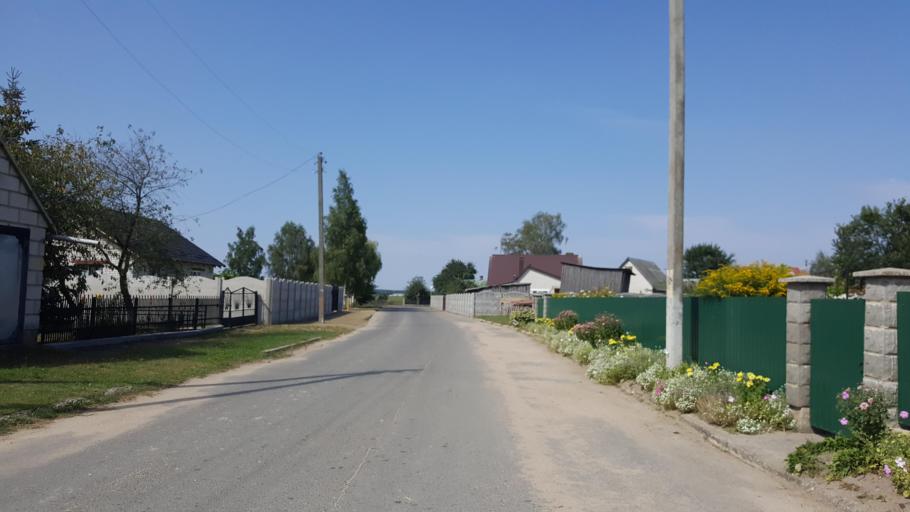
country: PL
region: Podlasie
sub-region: Powiat hajnowski
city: Czeremcha
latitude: 52.4996
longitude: 23.5724
